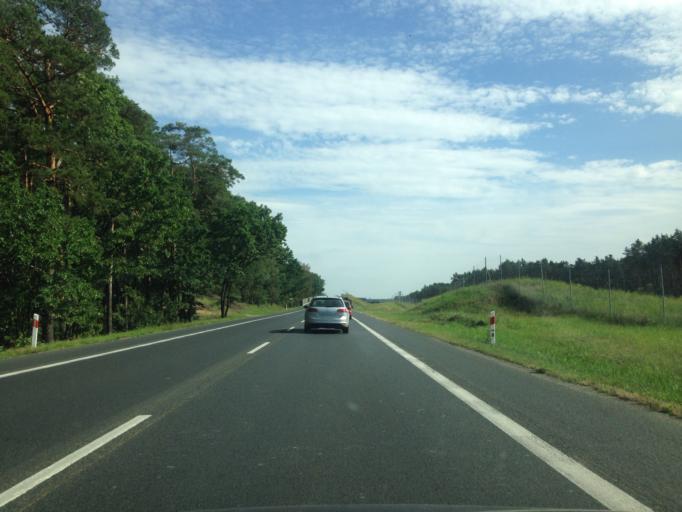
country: PL
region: Kujawsko-Pomorskie
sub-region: Powiat aleksandrowski
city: Aleksandrow Kujawski
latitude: 52.9185
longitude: 18.7139
